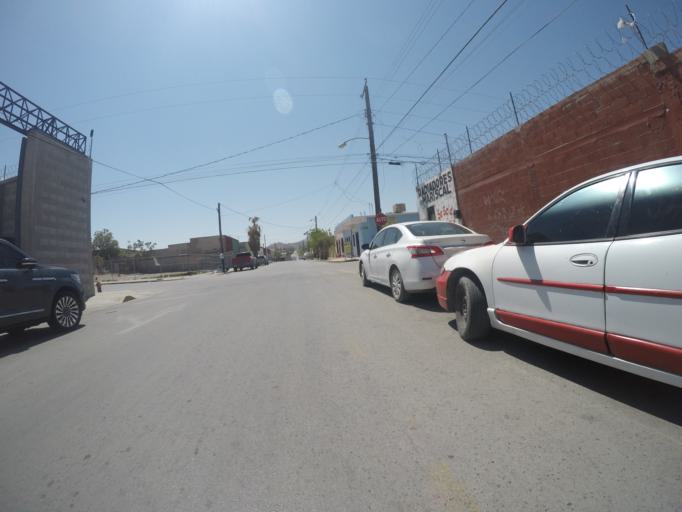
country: MX
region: Chihuahua
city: Ciudad Juarez
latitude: 31.7347
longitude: -106.4894
